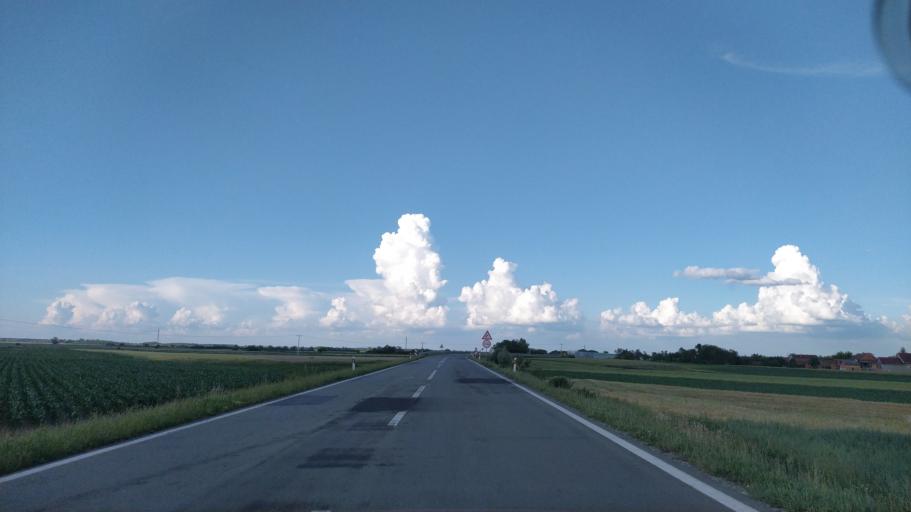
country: HR
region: Virovitick-Podravska
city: Slatina
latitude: 45.7286
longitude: 17.6511
